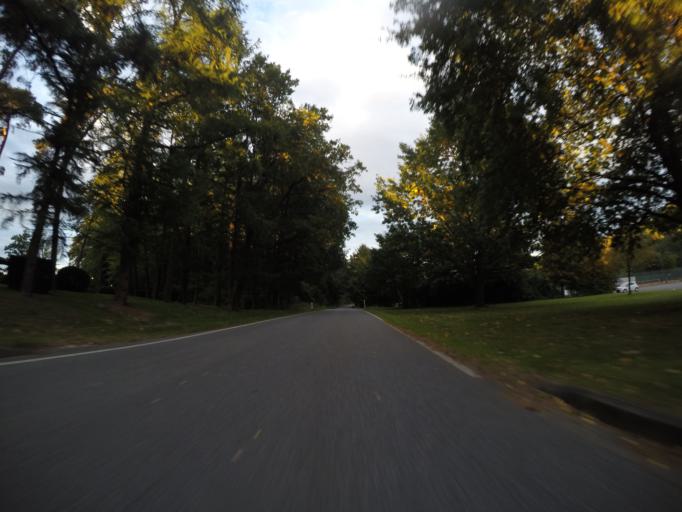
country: DE
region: Rheinland-Pfalz
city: Stebach
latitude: 50.5084
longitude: 7.6470
